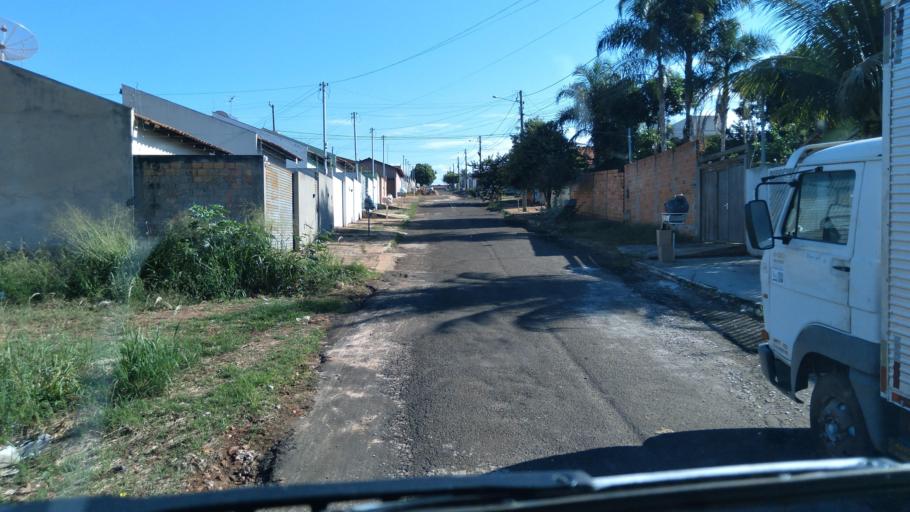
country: BR
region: Goias
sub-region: Mineiros
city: Mineiros
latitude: -17.5728
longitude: -52.5722
